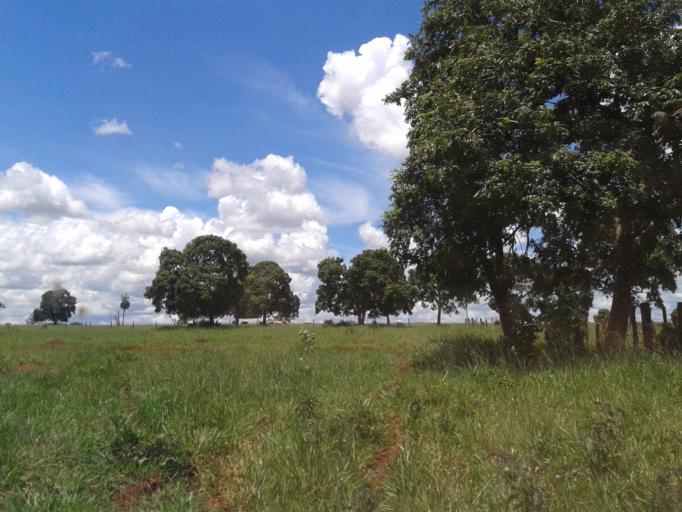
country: BR
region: Minas Gerais
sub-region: Santa Vitoria
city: Santa Vitoria
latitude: -18.7922
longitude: -49.8617
